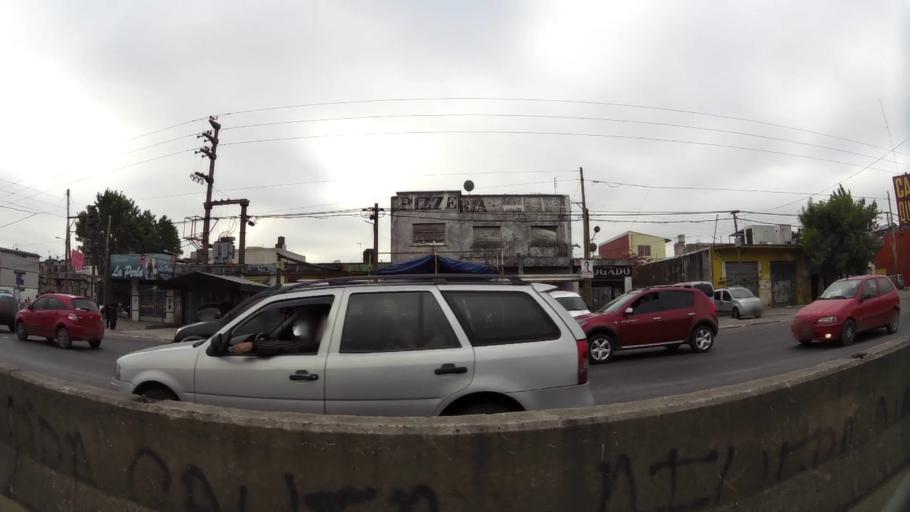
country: AR
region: Buenos Aires
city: San Justo
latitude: -34.6937
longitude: -58.5735
